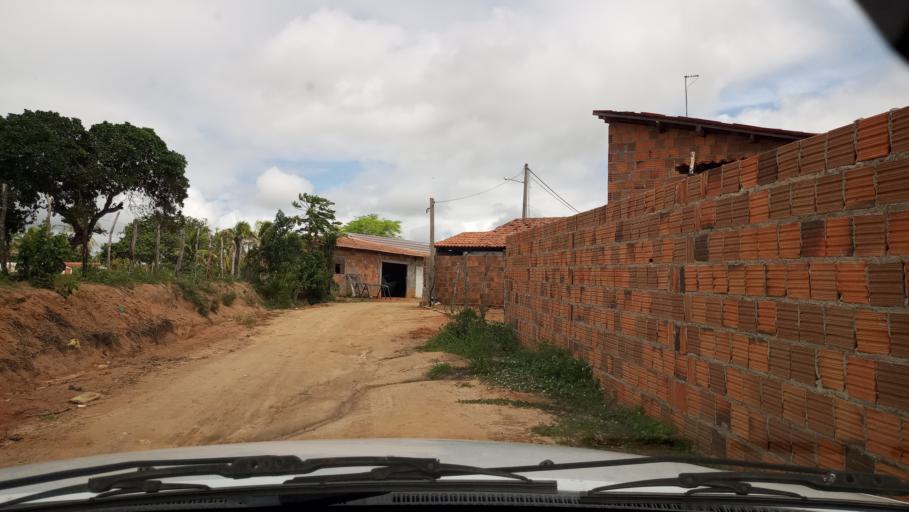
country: BR
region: Rio Grande do Norte
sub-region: Brejinho
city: Brejinho
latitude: -6.1587
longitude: -35.4414
